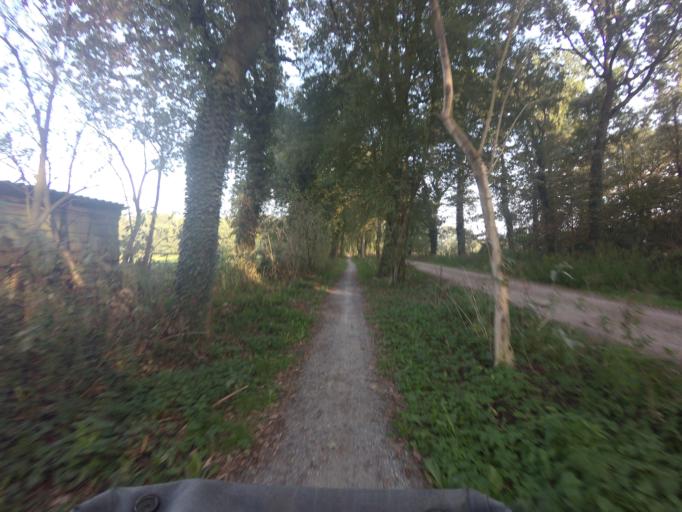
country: NL
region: Drenthe
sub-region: Gemeente Tynaarlo
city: Vries
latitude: 53.1081
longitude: 6.5259
